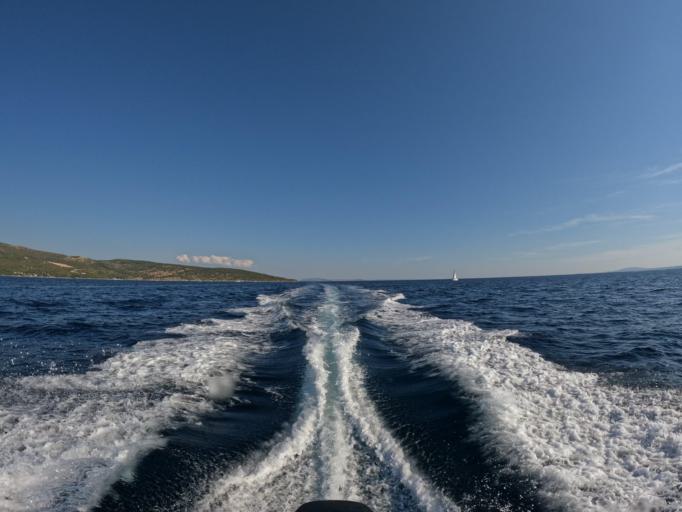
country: HR
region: Primorsko-Goranska
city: Punat
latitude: 44.9976
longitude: 14.6003
